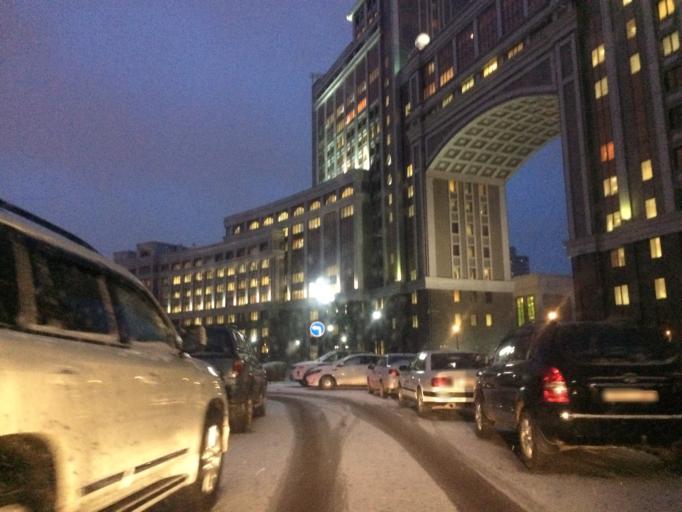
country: KZ
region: Astana Qalasy
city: Astana
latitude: 51.1318
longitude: 71.4129
